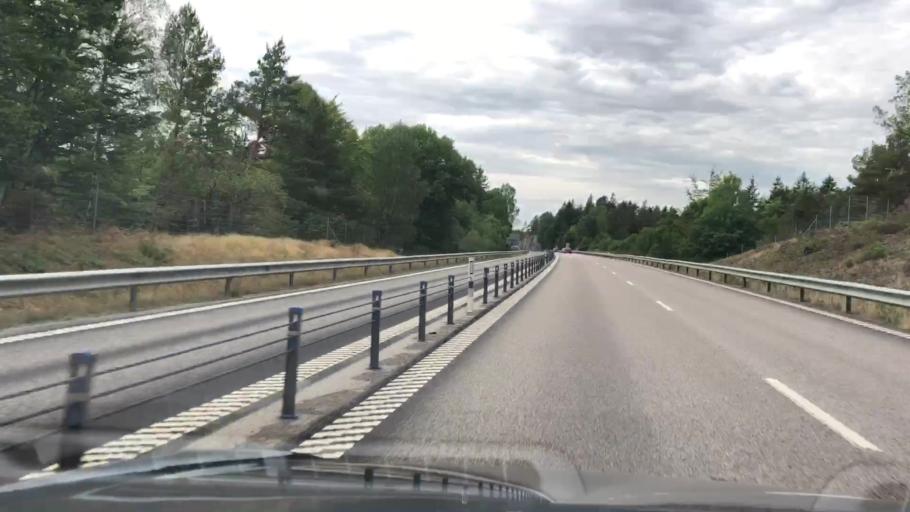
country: SE
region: Blekinge
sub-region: Ronneby Kommun
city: Brakne-Hoby
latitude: 56.2034
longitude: 14.9944
